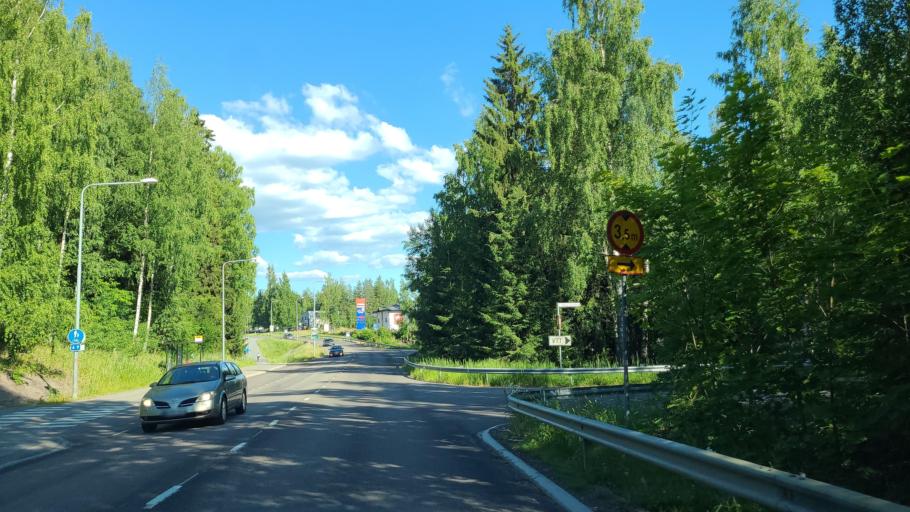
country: FI
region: Central Finland
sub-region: Jyvaeskylae
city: Jyvaeskylae
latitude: 62.2415
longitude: 25.8029
